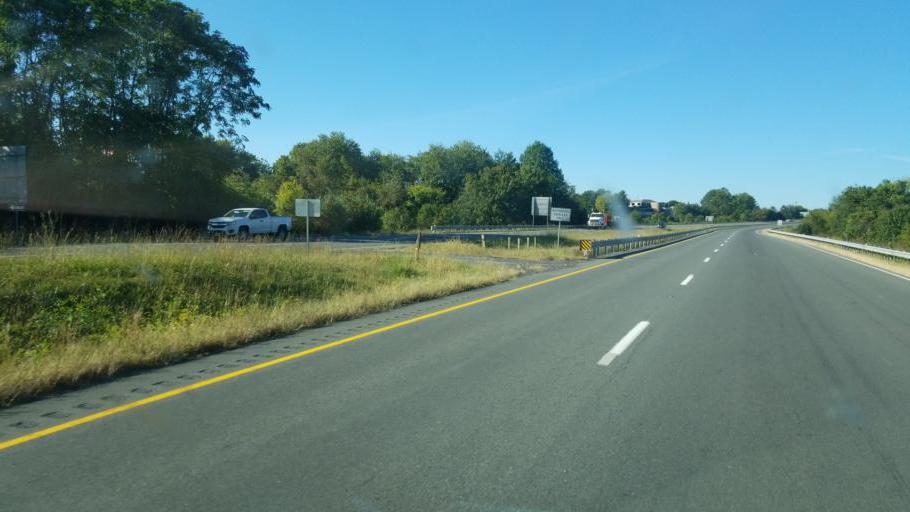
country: US
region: Virginia
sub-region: Culpeper County
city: Culpeper
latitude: 38.4481
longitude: -77.9868
